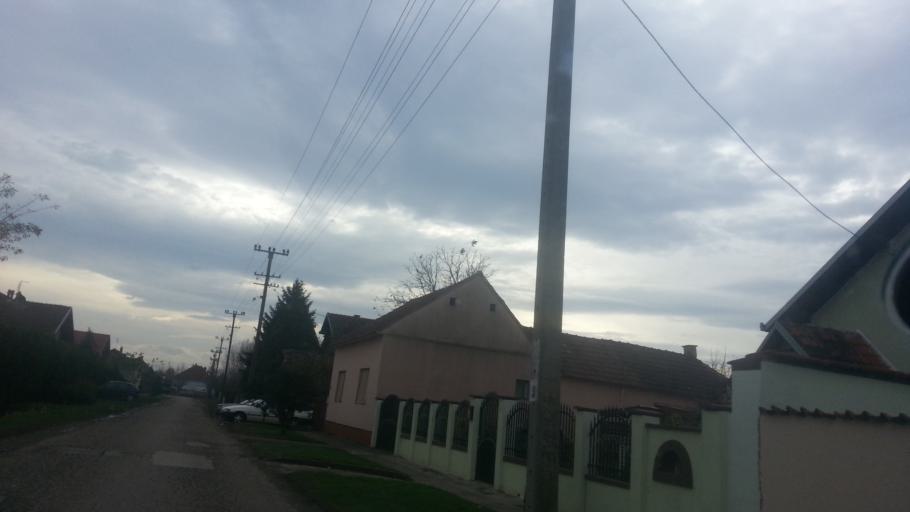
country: RS
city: Golubinci
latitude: 44.9839
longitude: 20.0574
